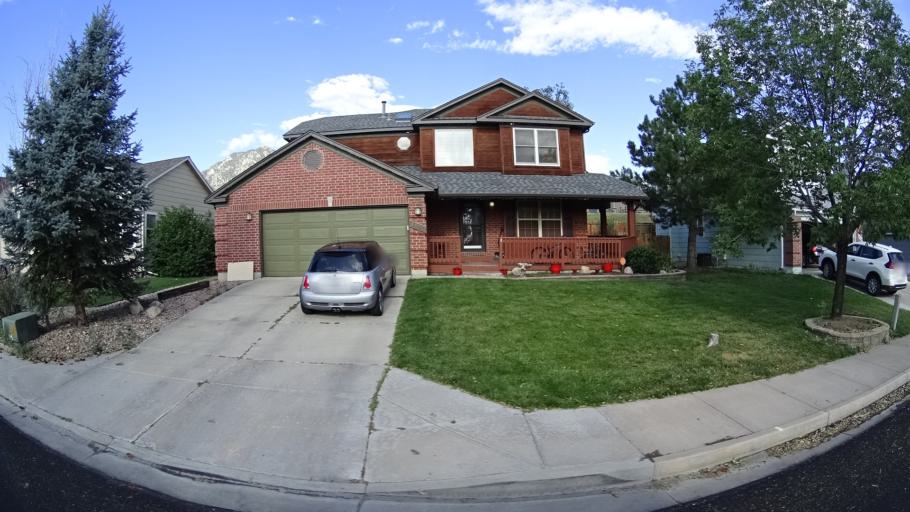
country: US
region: Colorado
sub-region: El Paso County
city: Fort Carson
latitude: 38.7566
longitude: -104.8127
